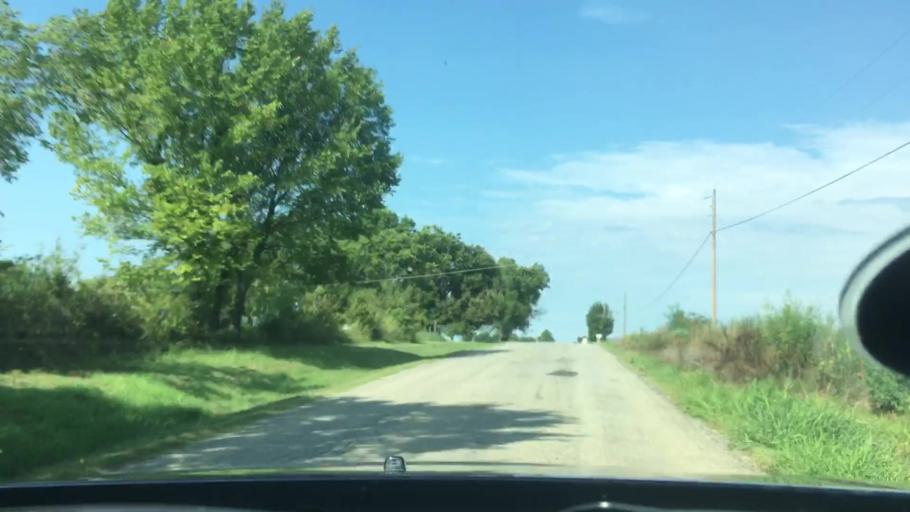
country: US
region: Oklahoma
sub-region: Bryan County
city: Colbert
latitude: 33.9110
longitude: -96.4900
